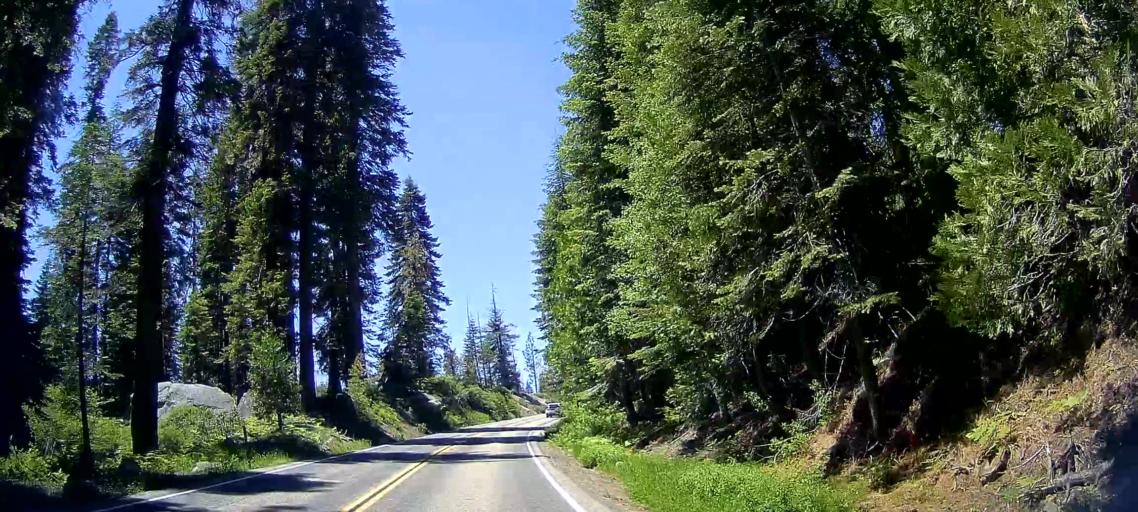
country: US
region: California
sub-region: Tulare County
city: Three Rivers
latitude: 36.6050
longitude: -118.7497
